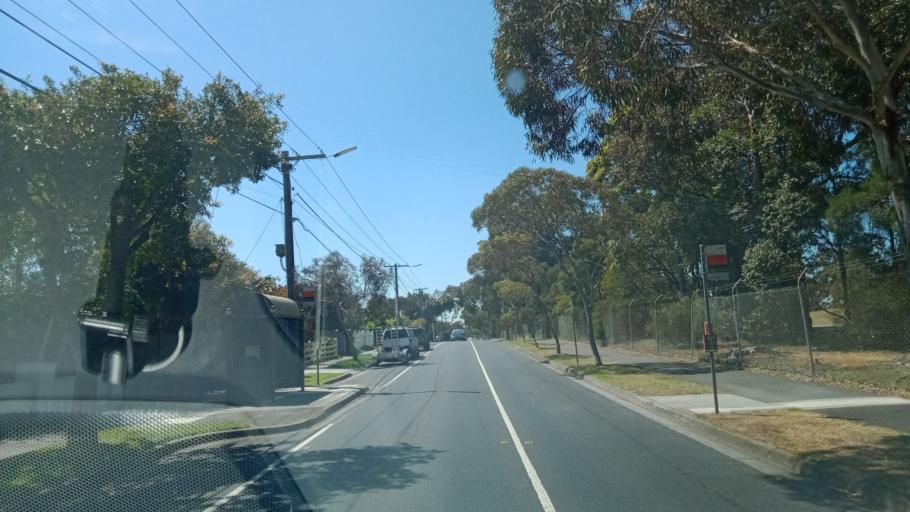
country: AU
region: Victoria
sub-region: Monash
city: Oakleigh South
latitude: -37.9154
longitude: 145.0886
